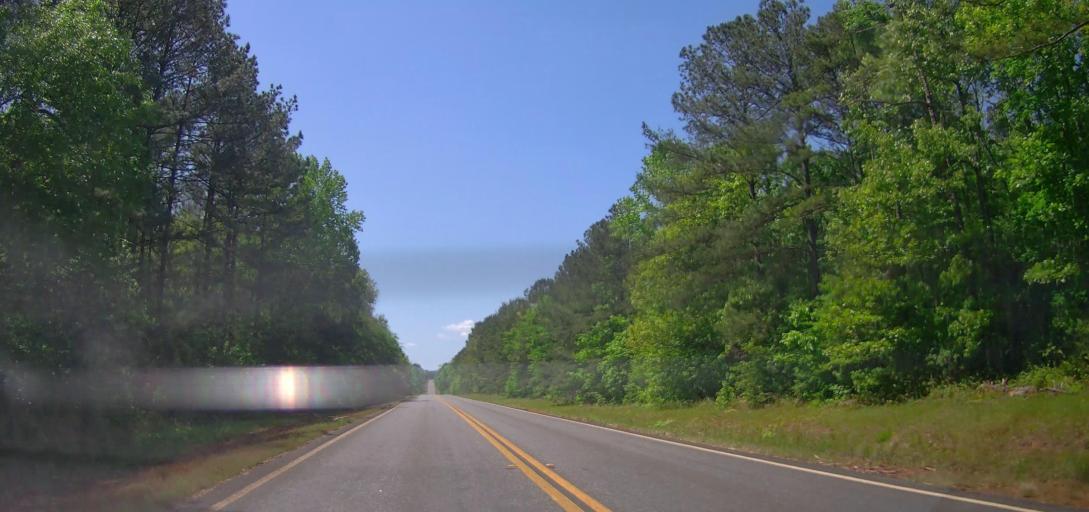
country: US
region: Georgia
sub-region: Putnam County
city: Eatonton
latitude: 33.2334
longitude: -83.5293
